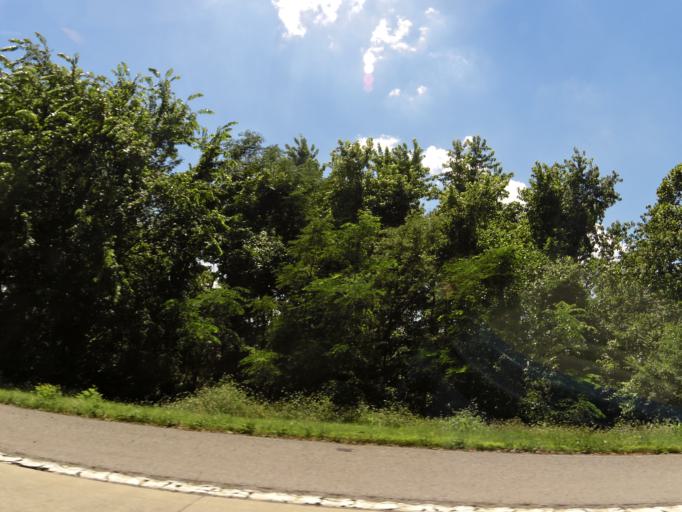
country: US
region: Missouri
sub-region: Pemiscot County
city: Caruthersville
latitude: 36.1257
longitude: -89.6194
